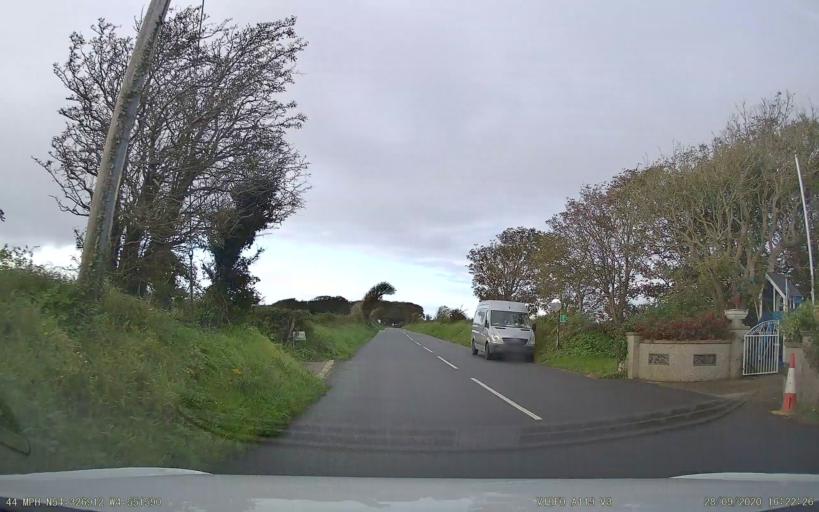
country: IM
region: Ramsey
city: Ramsey
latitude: 54.3269
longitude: -4.5516
